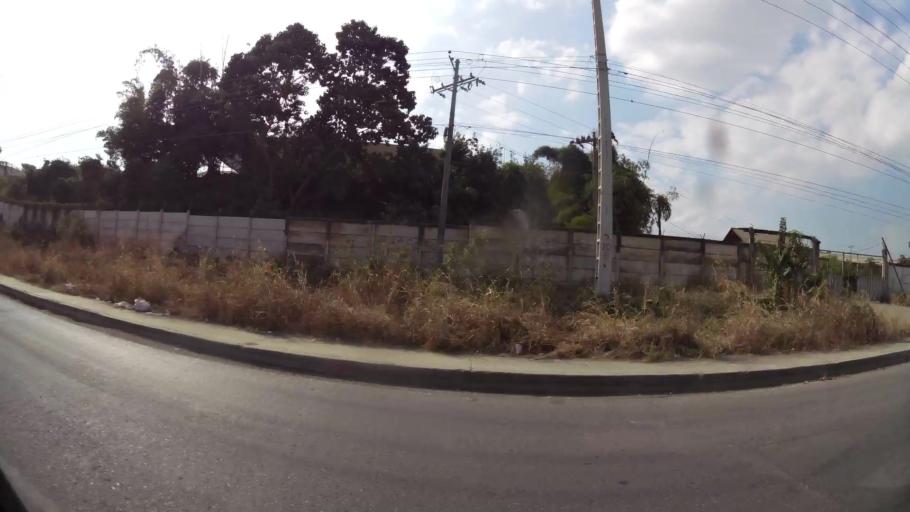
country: EC
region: Guayas
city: Santa Lucia
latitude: -2.1210
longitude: -79.9814
